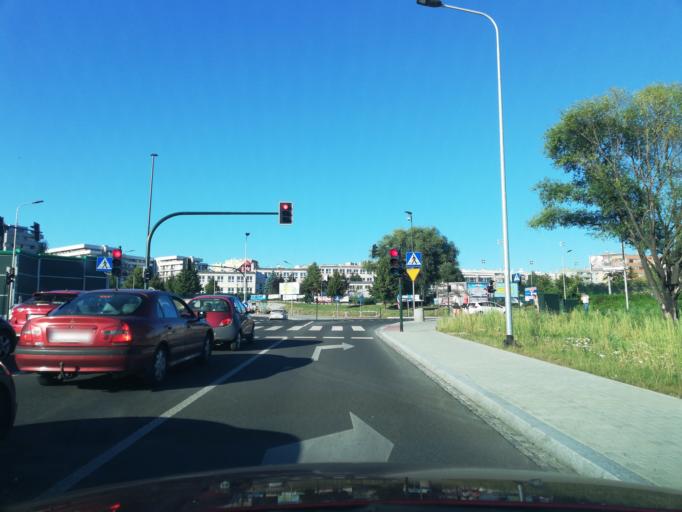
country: PL
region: Lesser Poland Voivodeship
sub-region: Krakow
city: Krakow
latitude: 50.0888
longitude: 19.9878
